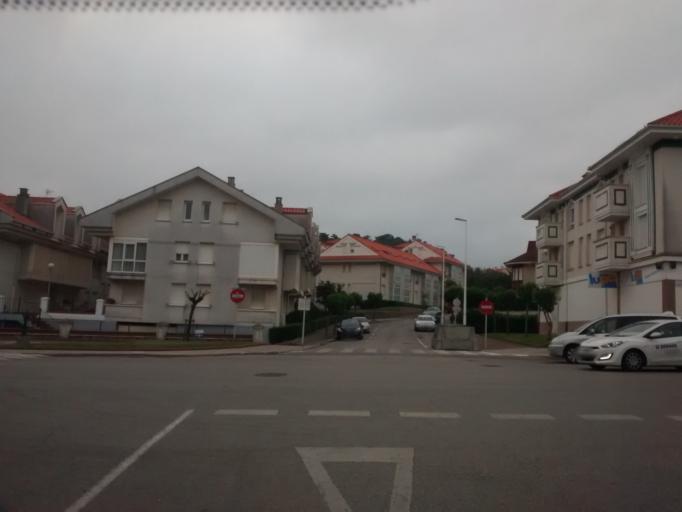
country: ES
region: Cantabria
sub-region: Provincia de Cantabria
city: Santander
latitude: 43.4548
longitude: -3.7425
